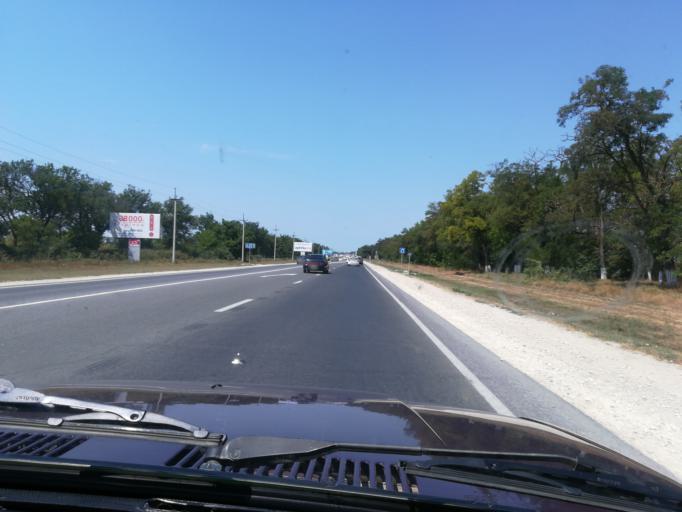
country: RU
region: Krasnodarskiy
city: Tsibanobalka
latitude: 44.9897
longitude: 37.3219
